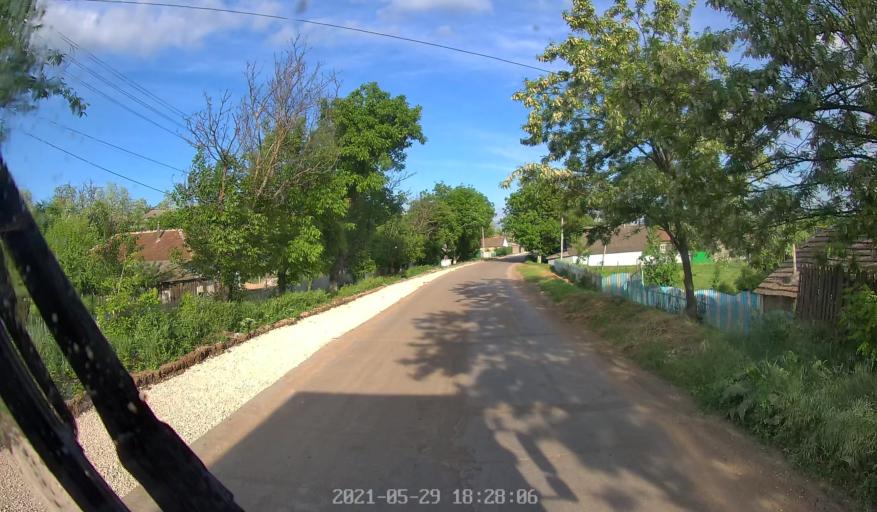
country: MD
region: Chisinau
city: Singera
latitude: 46.8294
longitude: 28.8645
